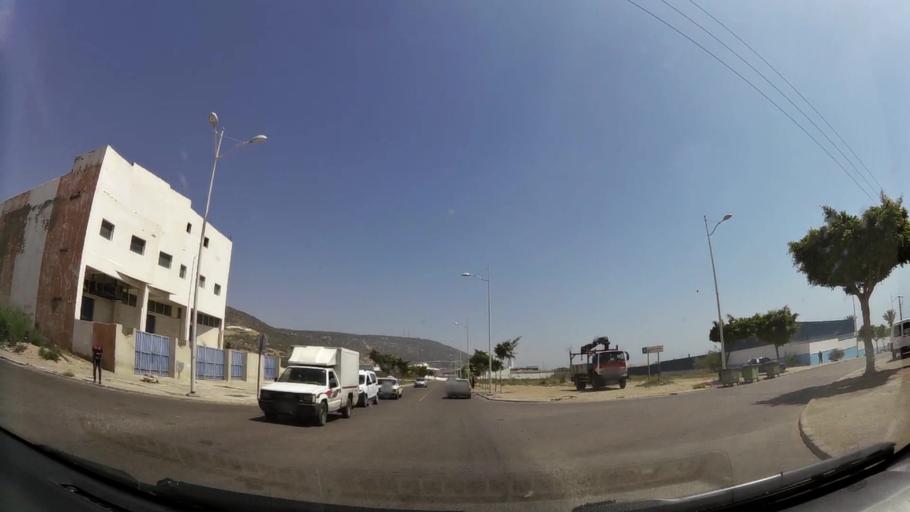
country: MA
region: Souss-Massa-Draa
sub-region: Agadir-Ida-ou-Tnan
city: Aourir
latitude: 30.4459
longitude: -9.6519
